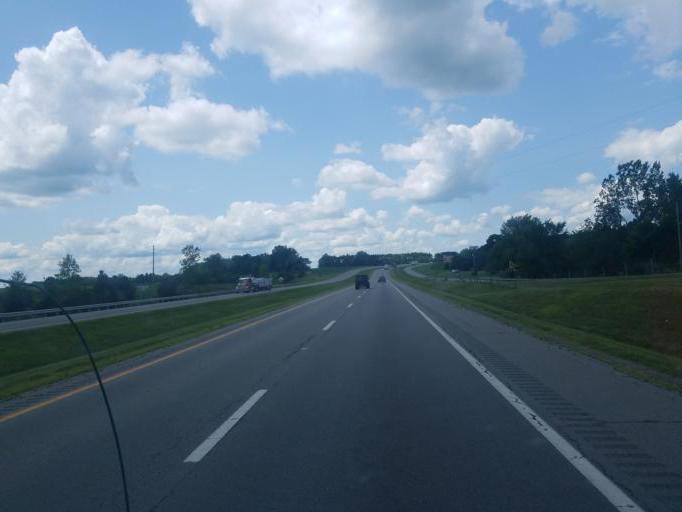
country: US
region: Ohio
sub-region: Wyandot County
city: Upper Sandusky
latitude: 40.7474
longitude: -83.2230
